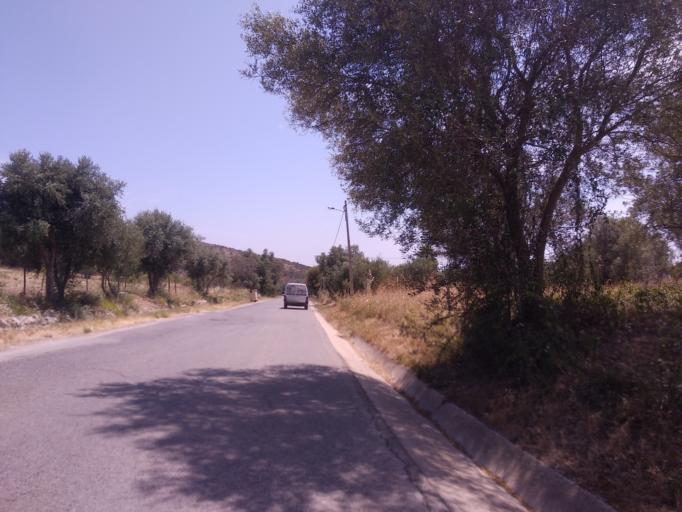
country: PT
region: Faro
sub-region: Faro
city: Santa Barbara de Nexe
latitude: 37.1137
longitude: -7.9458
